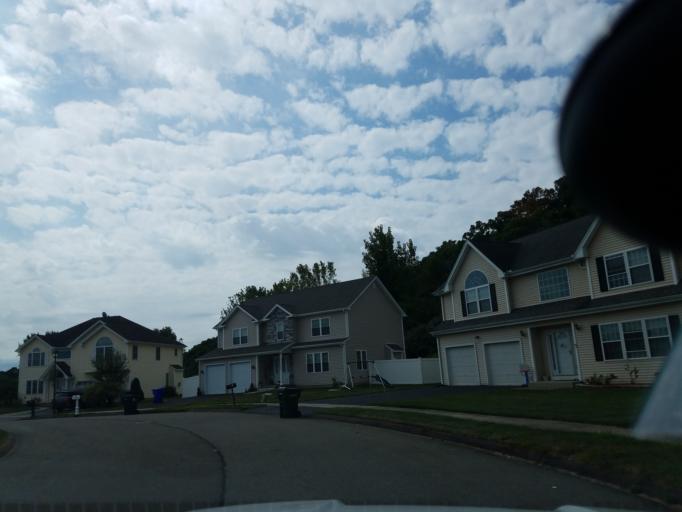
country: US
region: Connecticut
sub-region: Middlesex County
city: Cromwell
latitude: 41.6511
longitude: -72.6369
